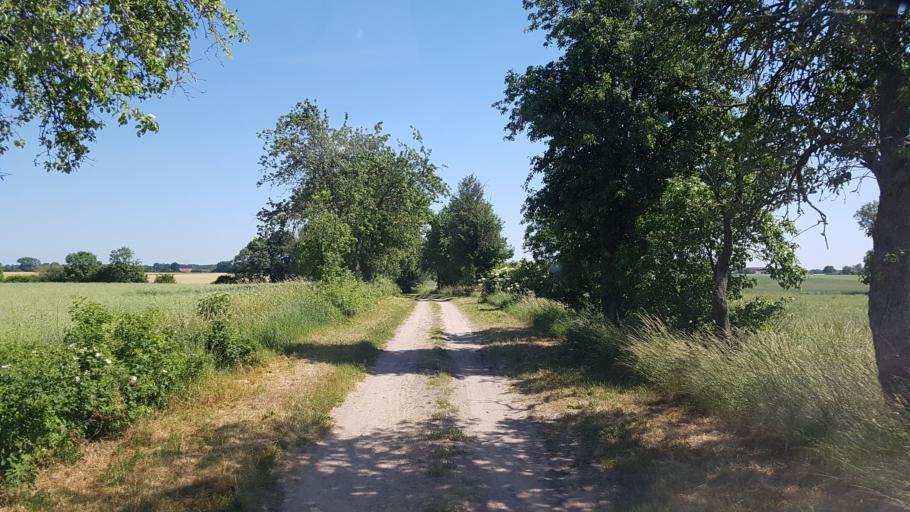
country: DE
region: Brandenburg
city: Sonnewalde
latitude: 51.7006
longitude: 13.6674
